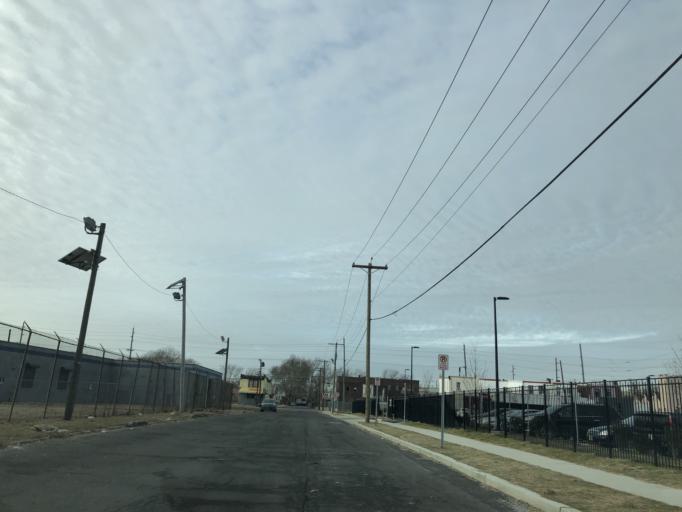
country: US
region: New Jersey
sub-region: Camden County
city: Camden
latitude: 39.9282
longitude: -75.1180
